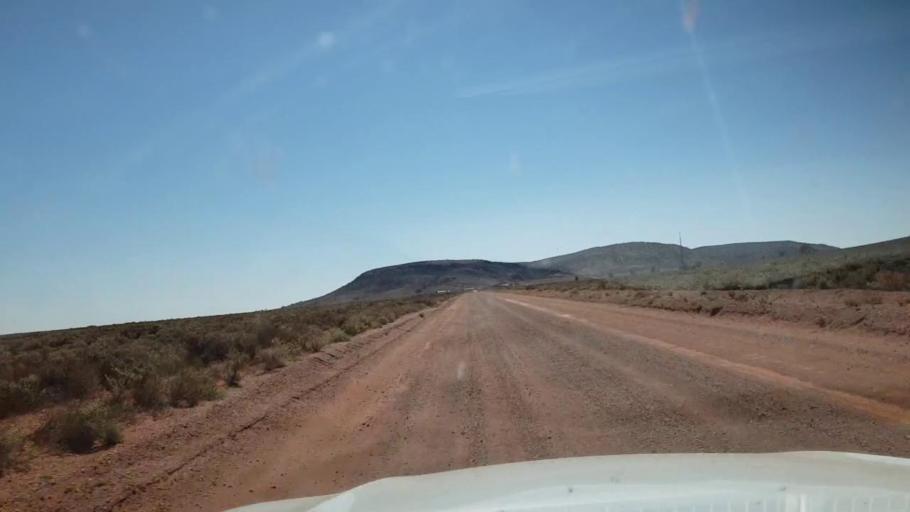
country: AU
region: South Australia
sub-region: Whyalla
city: Whyalla
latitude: -32.7017
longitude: 137.1349
